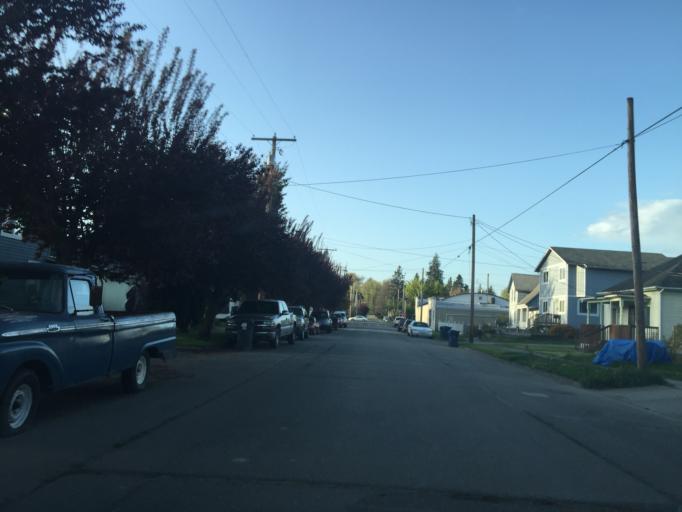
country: US
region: Washington
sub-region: Skagit County
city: Mount Vernon
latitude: 48.4205
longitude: -122.3435
